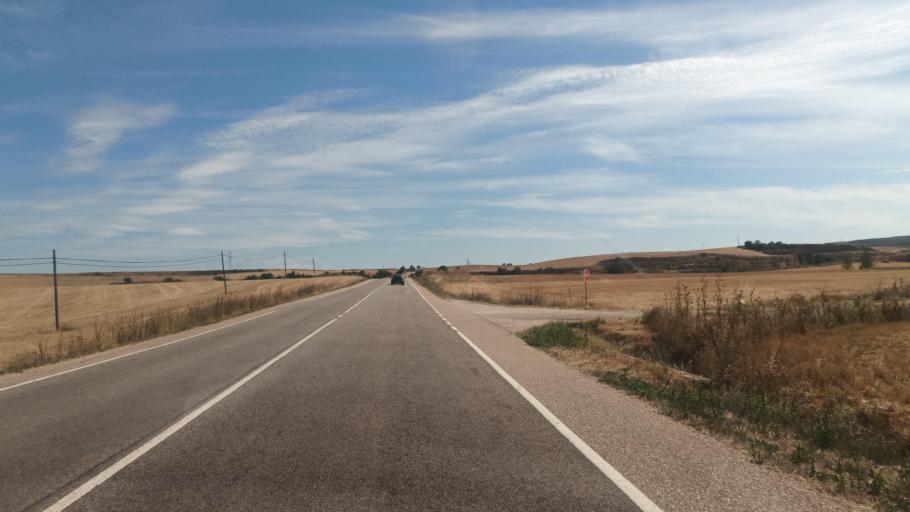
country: ES
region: Castille and Leon
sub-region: Provincia de Burgos
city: Aguilar de Bureba
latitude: 42.5800
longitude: -3.3354
